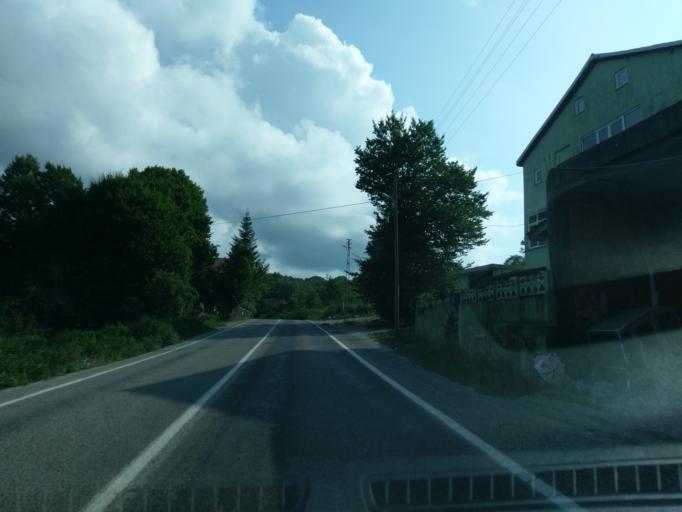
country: TR
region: Sinop
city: Ayancik
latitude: 41.8785
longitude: 34.5106
